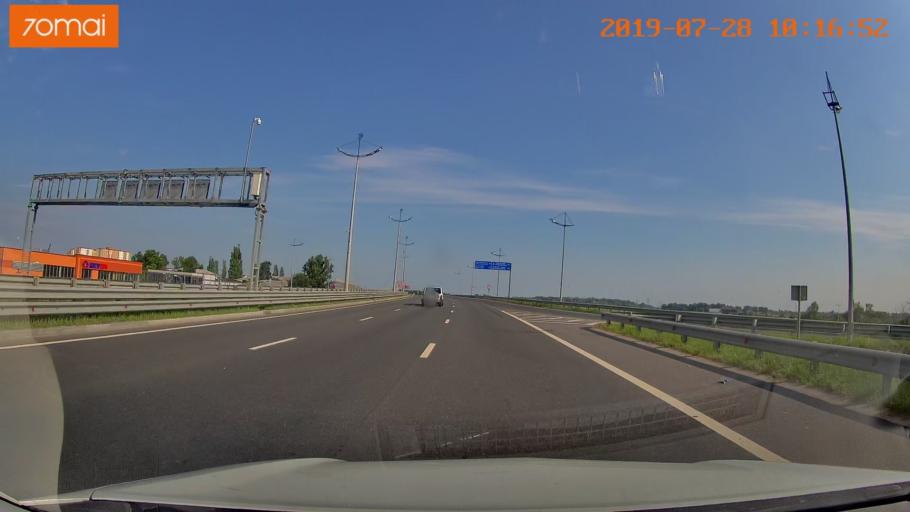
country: RU
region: Kaliningrad
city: Maloye Isakovo
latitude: 54.7319
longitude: 20.5978
